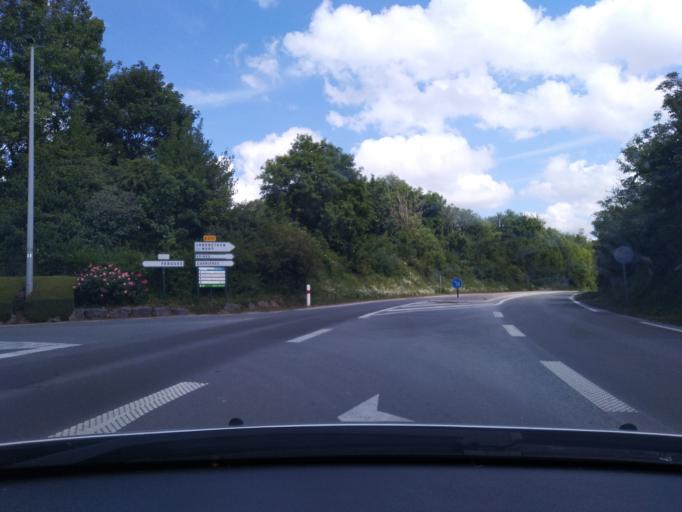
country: FR
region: Nord-Pas-de-Calais
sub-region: Departement du Pas-de-Calais
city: Ferques
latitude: 50.8290
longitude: 1.7553
